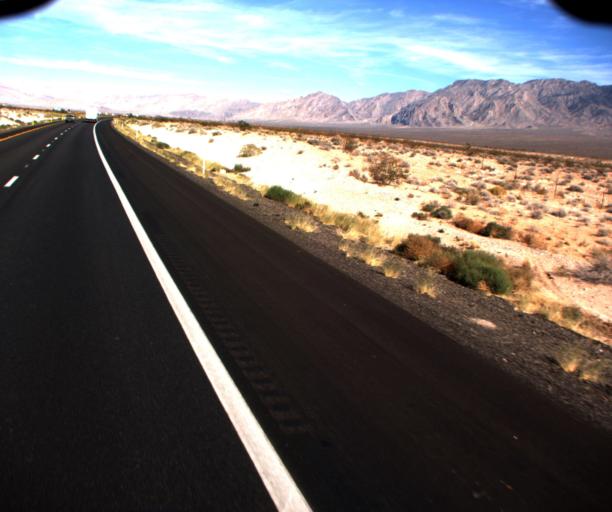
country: US
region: Arizona
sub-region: Mohave County
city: Beaver Dam
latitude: 36.8575
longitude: -113.9822
